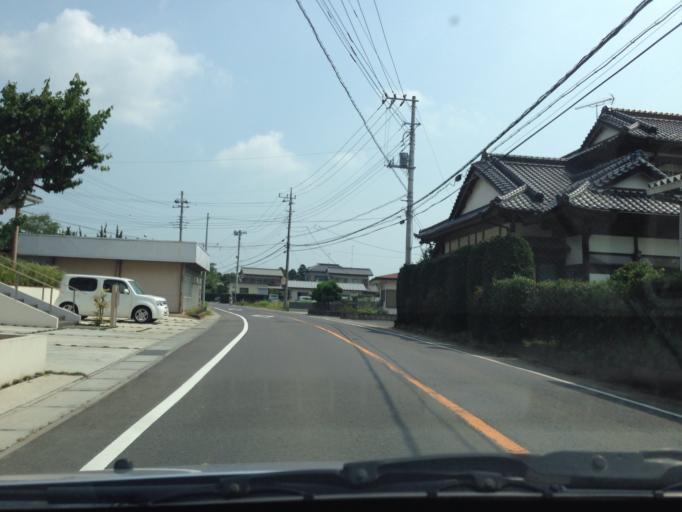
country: JP
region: Ibaraki
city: Inashiki
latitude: 36.0013
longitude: 140.3250
